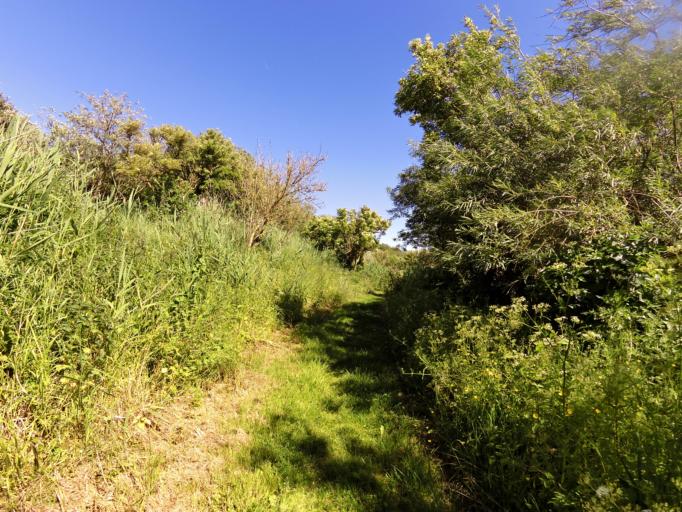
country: NL
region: South Holland
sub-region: Gemeente Goeree-Overflakkee
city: Goedereede
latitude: 51.8205
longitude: 4.0282
